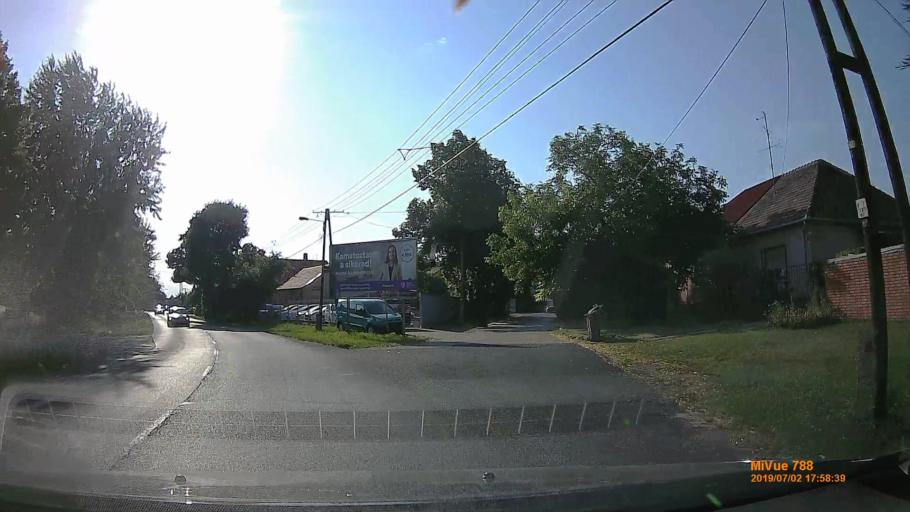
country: HU
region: Gyor-Moson-Sopron
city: Mosonmagyarovar
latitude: 47.8515
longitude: 17.2757
